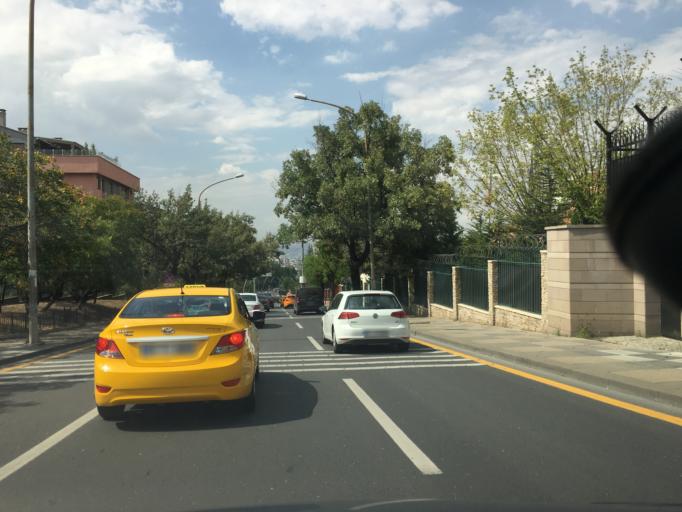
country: TR
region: Ankara
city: Cankaya
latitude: 39.8979
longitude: 32.8613
